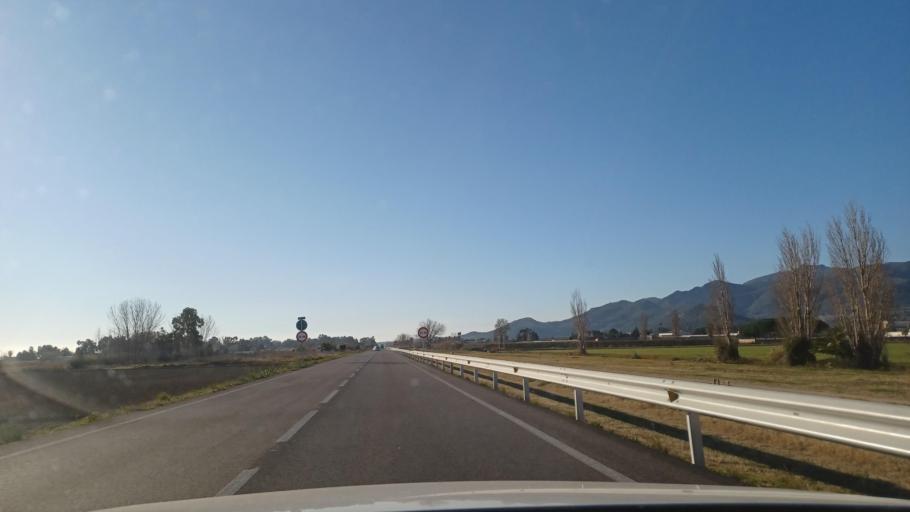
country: ES
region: Catalonia
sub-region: Provincia de Tarragona
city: Amposta
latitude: 40.6853
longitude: 0.5904
